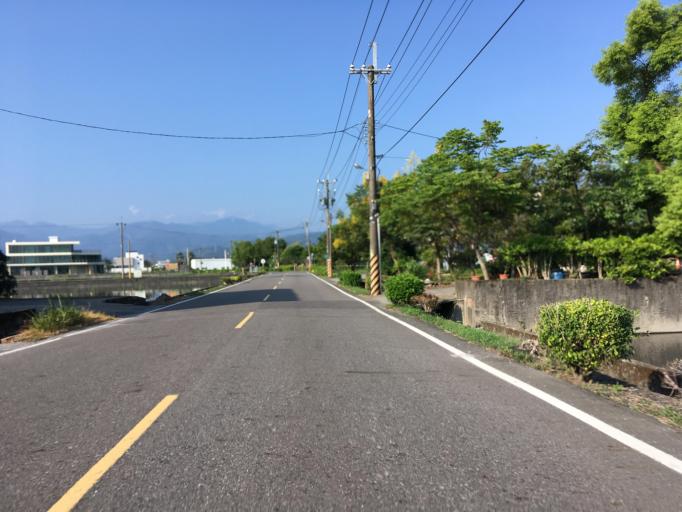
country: TW
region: Taiwan
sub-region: Yilan
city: Yilan
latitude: 24.6797
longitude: 121.7359
